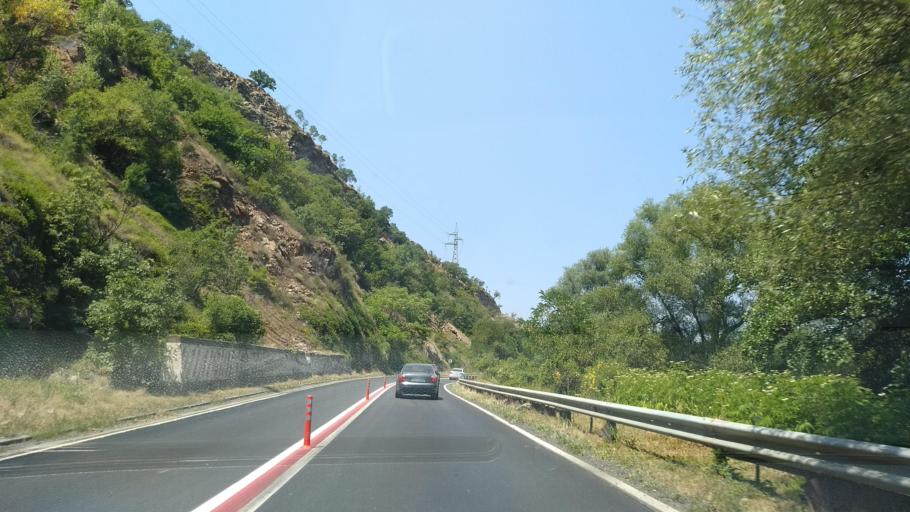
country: BG
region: Blagoevgrad
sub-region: Obshtina Kresna
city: Stara Kresna
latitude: 41.8401
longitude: 23.1505
